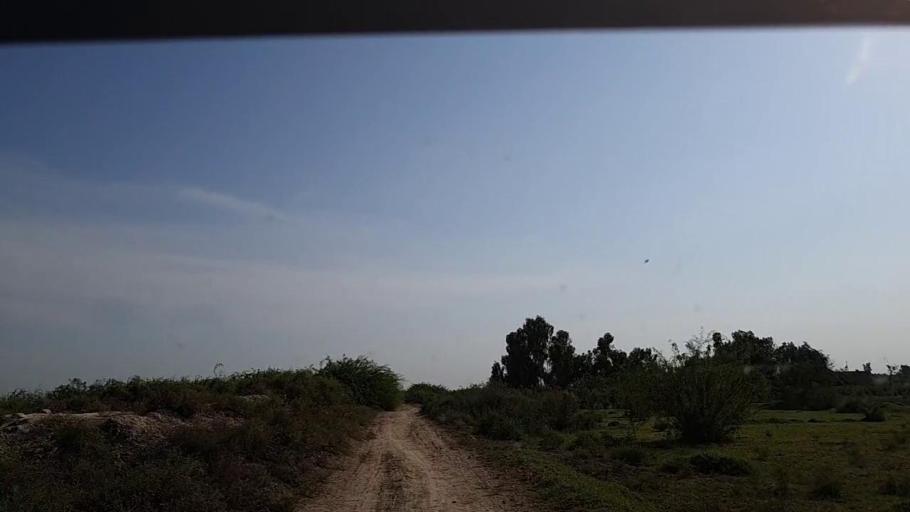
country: PK
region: Sindh
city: Adilpur
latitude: 27.9036
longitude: 69.2329
